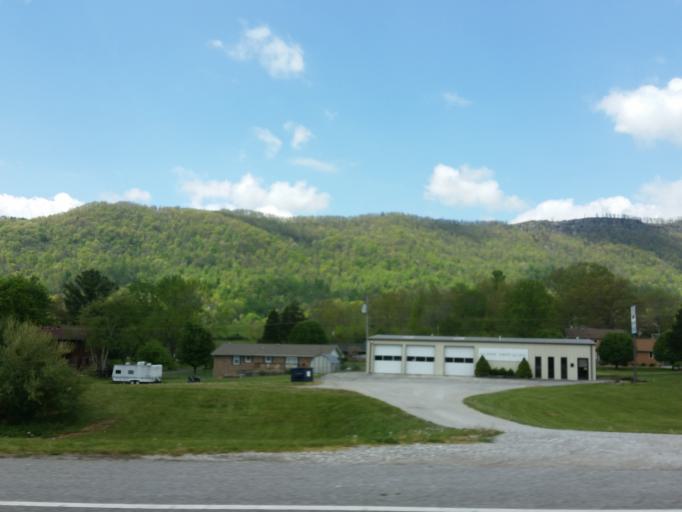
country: US
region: Tennessee
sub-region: Campbell County
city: Fincastle
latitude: 36.4094
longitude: -84.0592
